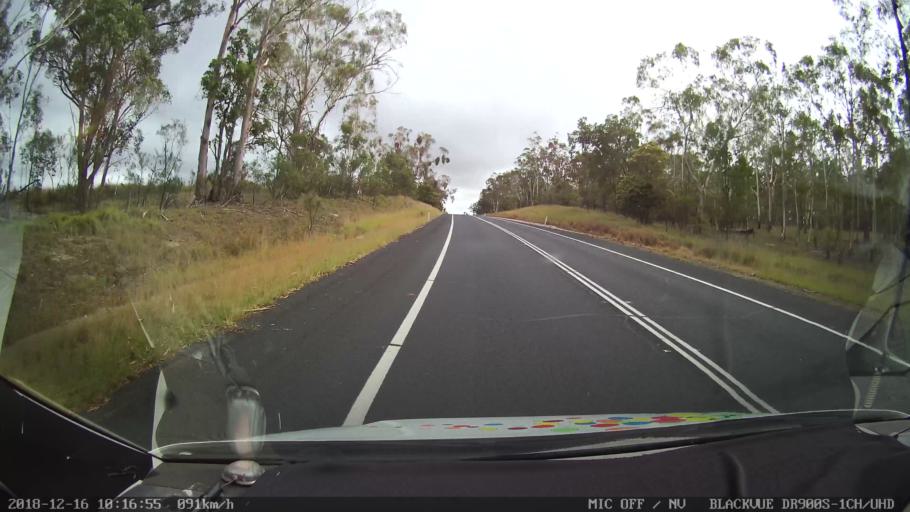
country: AU
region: New South Wales
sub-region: Tenterfield Municipality
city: Carrolls Creek
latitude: -29.2620
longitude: 151.9876
